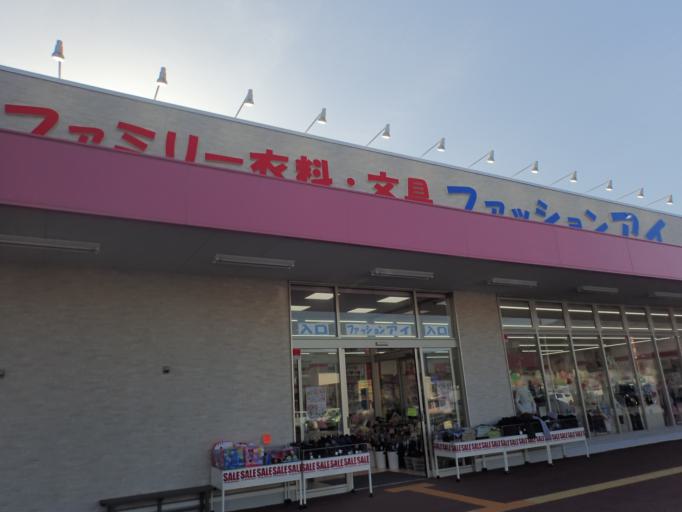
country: JP
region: Iwate
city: Ofunato
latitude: 39.0596
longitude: 141.7217
